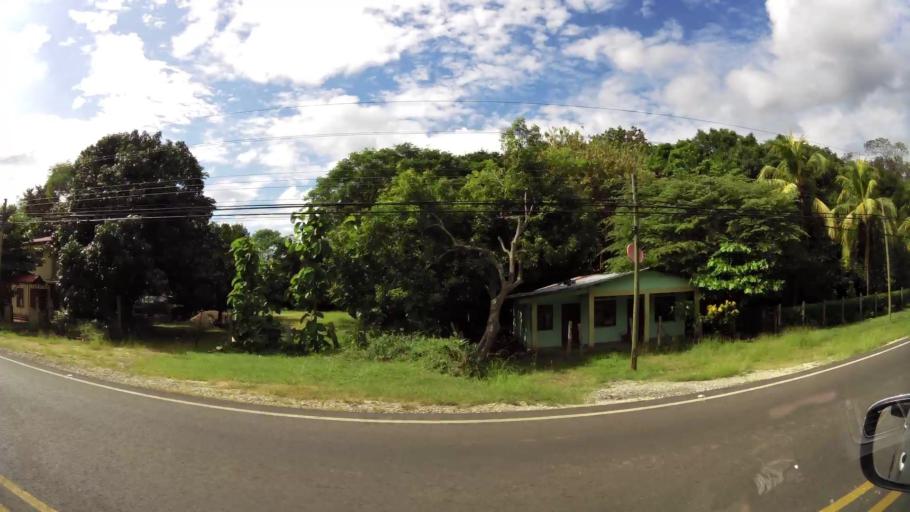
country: CR
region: Guanacaste
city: Hojancha
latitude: 10.1149
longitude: -85.3448
